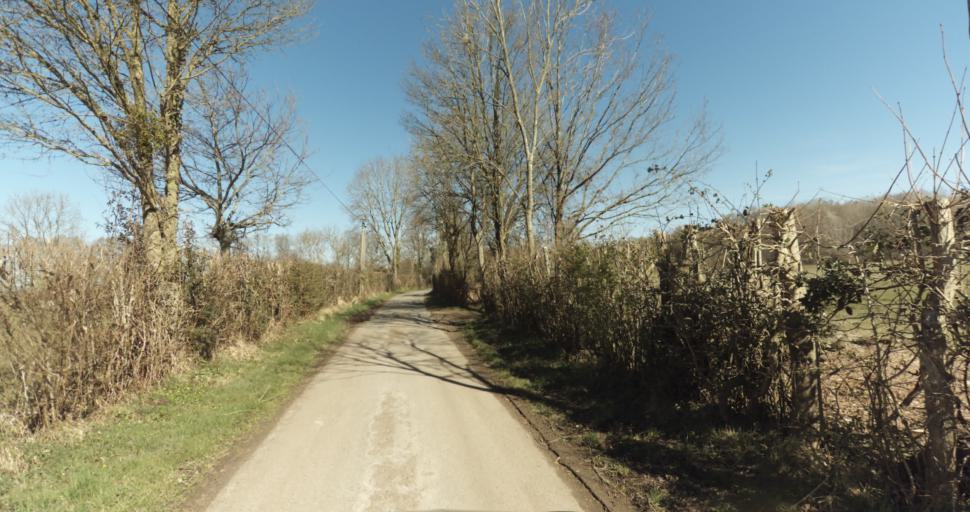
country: FR
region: Lower Normandy
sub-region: Departement du Calvados
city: Livarot
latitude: 48.9820
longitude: 0.0858
